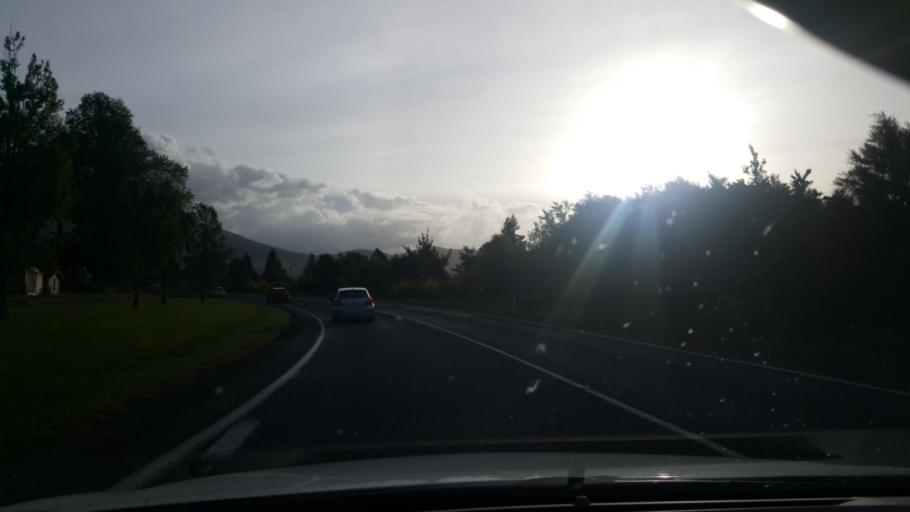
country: NZ
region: Waikato
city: Turangi
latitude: -38.9824
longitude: 175.8213
